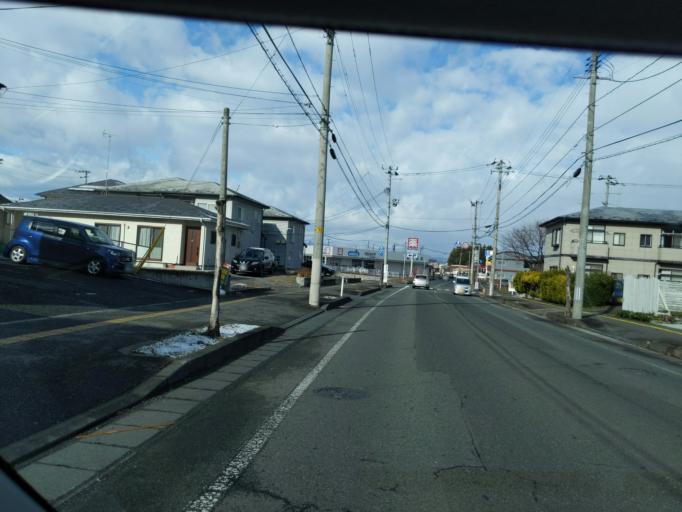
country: JP
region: Iwate
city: Mizusawa
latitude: 39.1230
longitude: 141.1306
